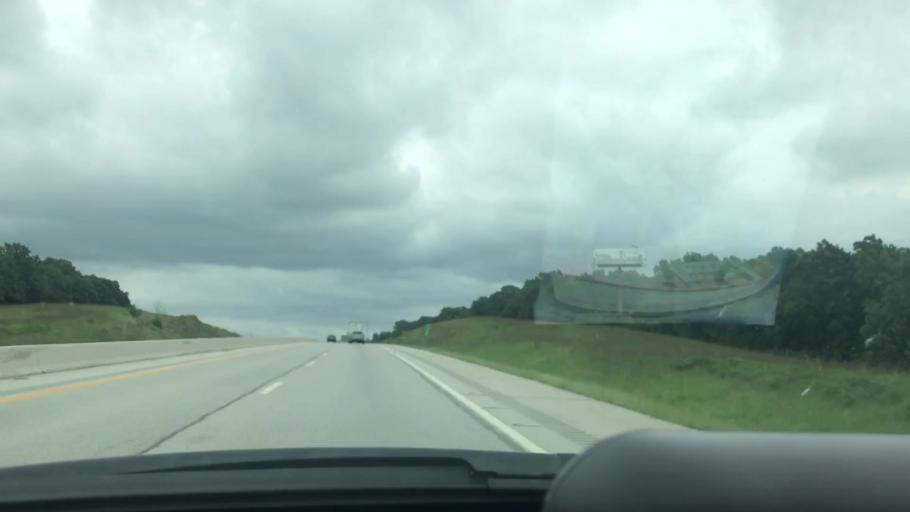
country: US
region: Kansas
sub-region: Cherokee County
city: Galena
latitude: 36.9789
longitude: -94.6390
